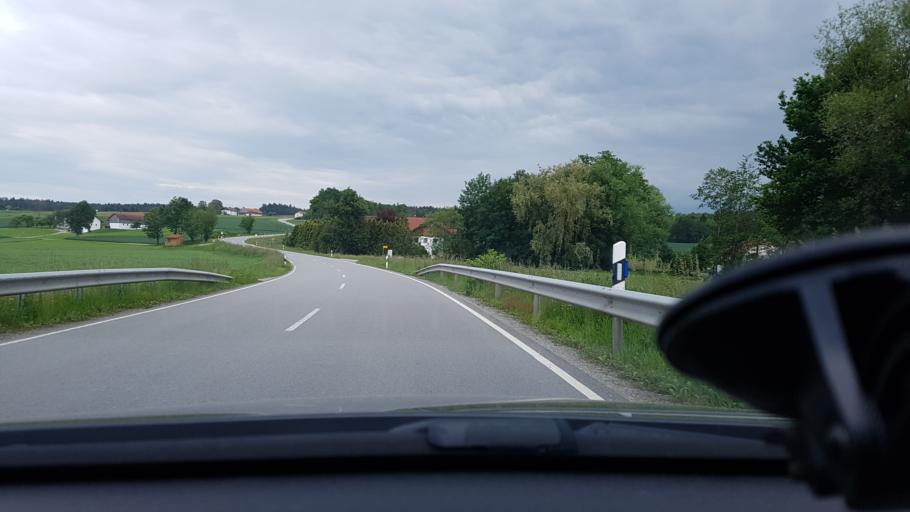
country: DE
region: Bavaria
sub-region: Lower Bavaria
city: Pfarrkirchen
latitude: 48.4157
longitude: 12.9556
